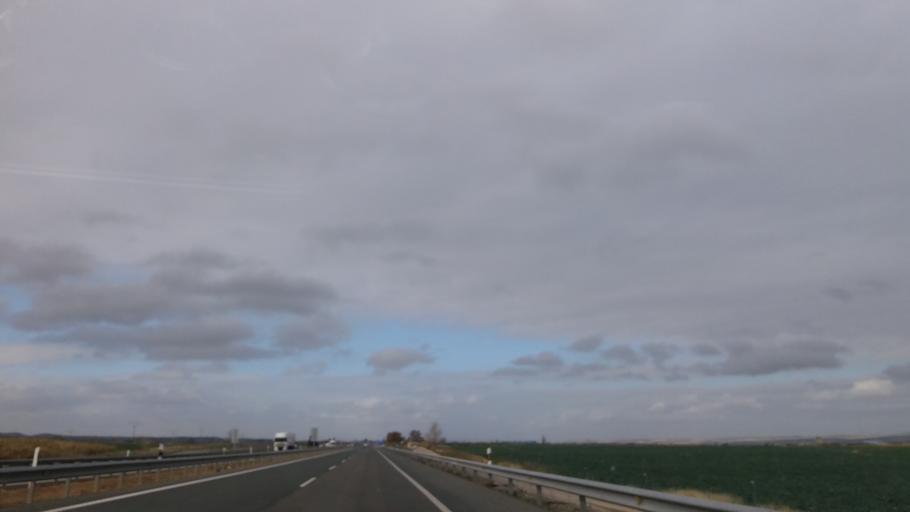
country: ES
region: Navarre
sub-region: Provincia de Navarra
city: Bunuel
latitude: 41.9477
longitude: -1.4793
